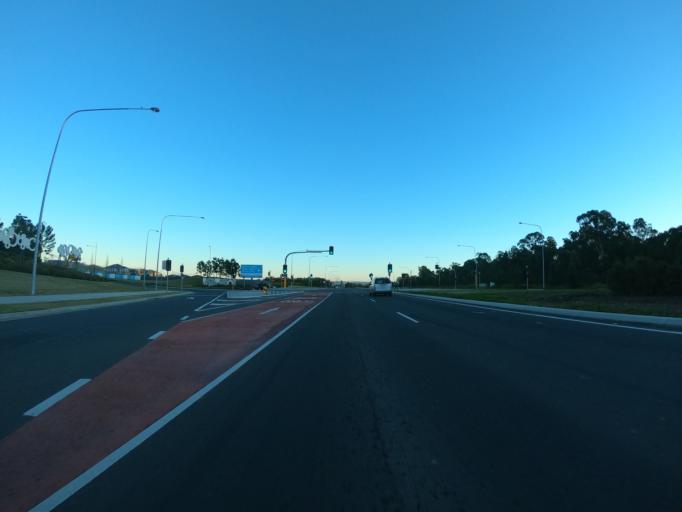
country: AU
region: New South Wales
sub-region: Blacktown
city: Riverstone
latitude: -33.6918
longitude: 150.8263
